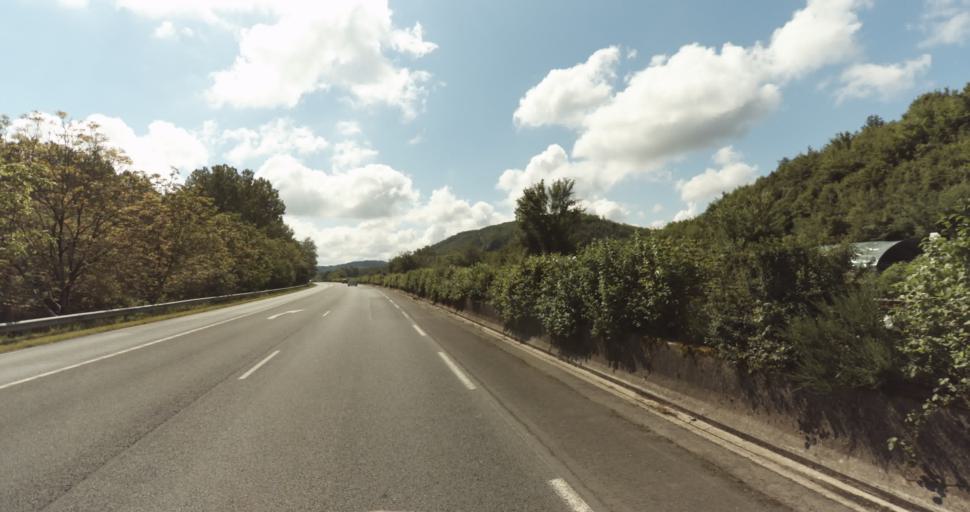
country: FR
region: Aquitaine
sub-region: Departement de la Dordogne
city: Belves
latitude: 44.8277
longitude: 0.9469
